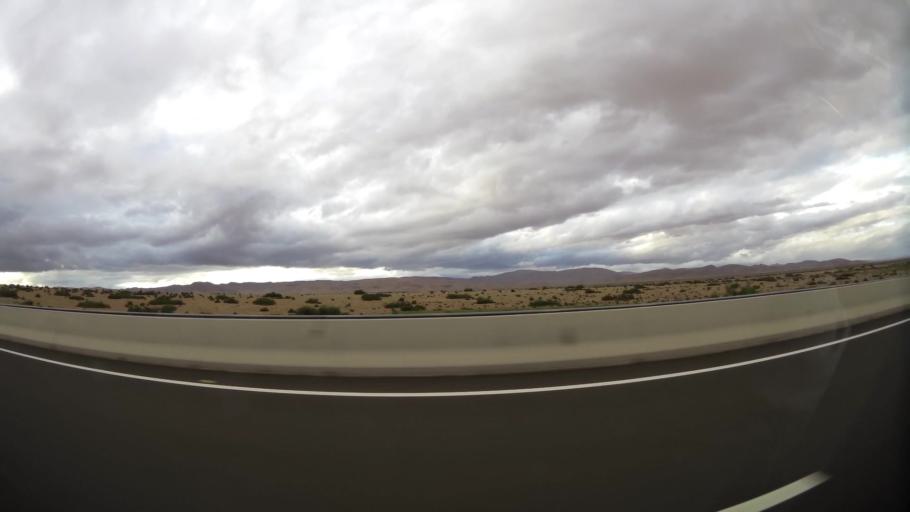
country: MA
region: Taza-Al Hoceima-Taounate
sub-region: Taza
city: Guercif
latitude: 34.3050
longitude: -3.6318
